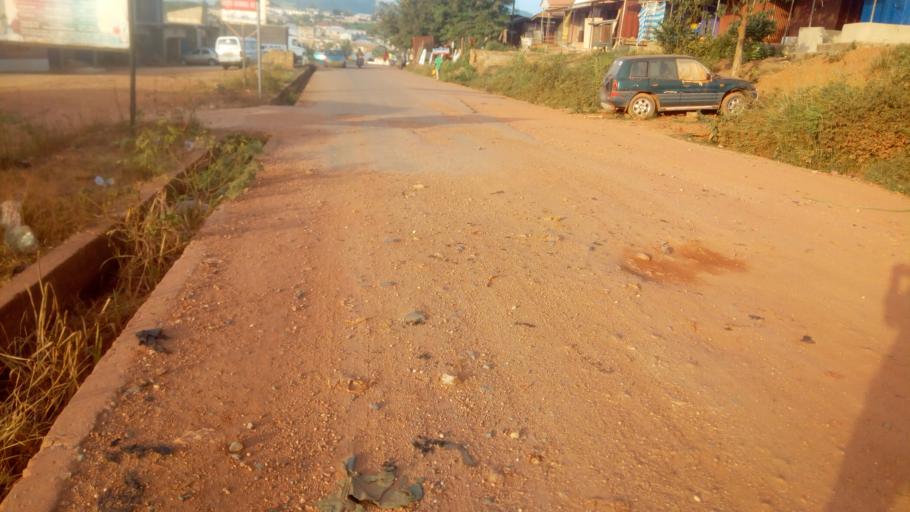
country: GH
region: Ashanti
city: Obuasi
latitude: 6.2128
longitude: -1.6989
